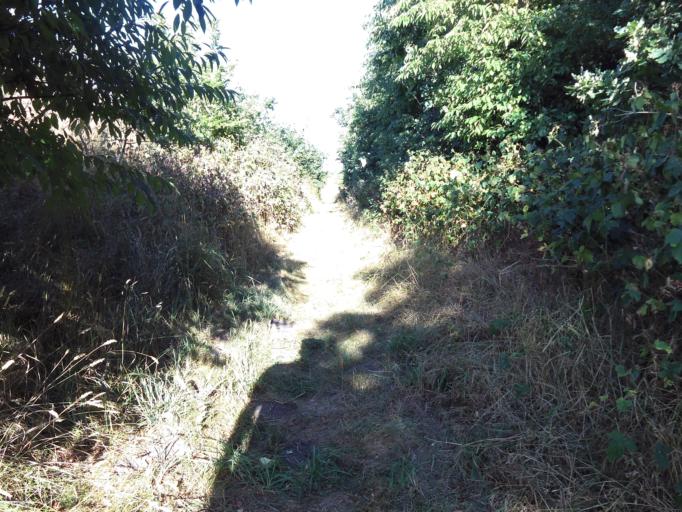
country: DK
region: South Denmark
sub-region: Aabenraa Kommune
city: Rodekro
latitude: 55.1018
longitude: 9.3421
